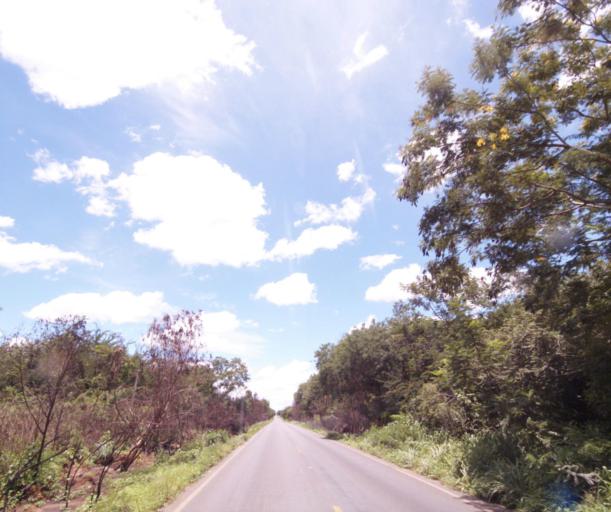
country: BR
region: Bahia
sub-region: Bom Jesus Da Lapa
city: Bom Jesus da Lapa
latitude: -13.2644
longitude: -43.5717
